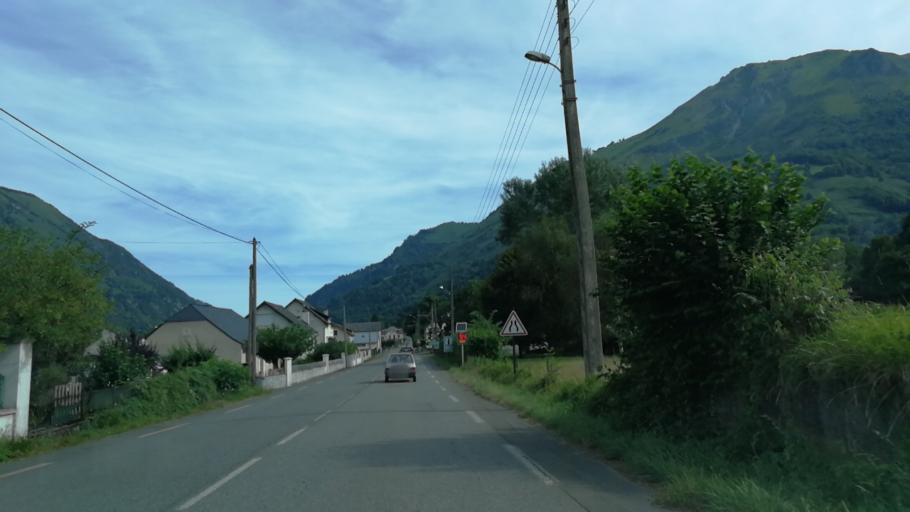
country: FR
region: Aquitaine
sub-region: Departement des Pyrenees-Atlantiques
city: Arette
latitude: 42.9909
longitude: -0.6031
